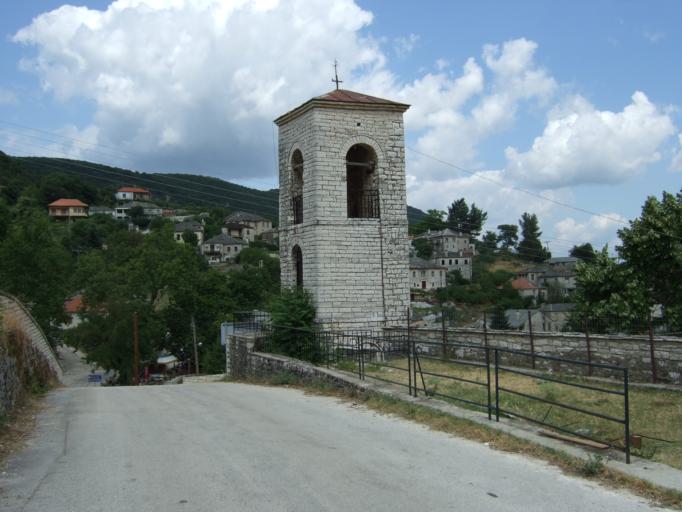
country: GR
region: Epirus
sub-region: Nomos Ioanninon
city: Kalpaki
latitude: 39.9335
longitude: 20.6727
